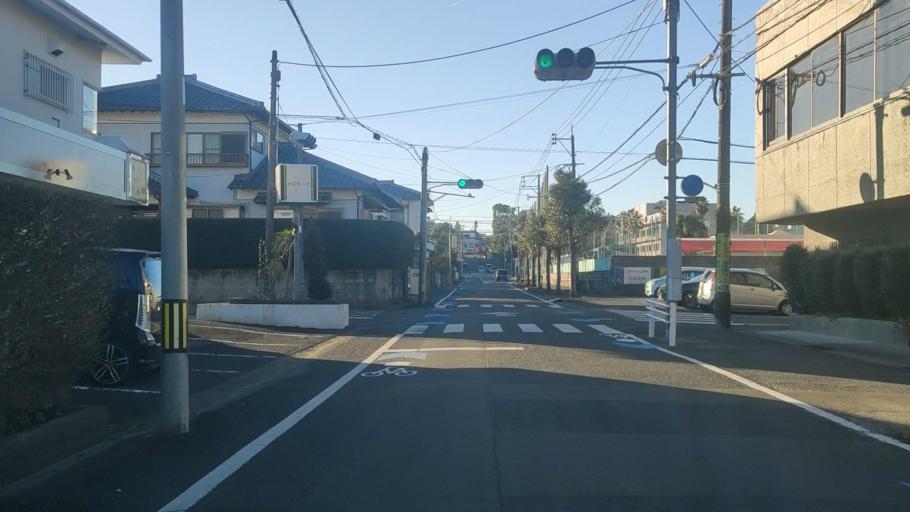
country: JP
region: Miyazaki
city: Miyazaki-shi
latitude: 31.9003
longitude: 131.4153
